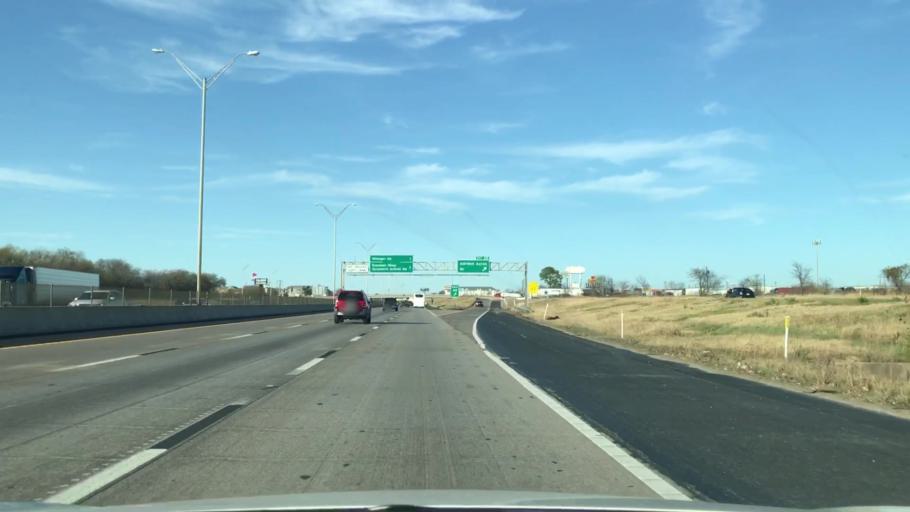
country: US
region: Texas
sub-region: Tarrant County
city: Crowley
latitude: 32.5933
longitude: -97.3194
